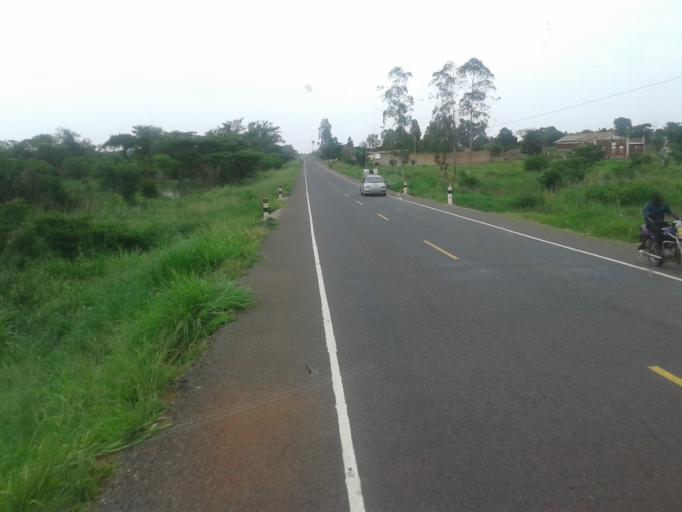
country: UG
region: Northern Region
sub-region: Oyam District
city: Oyam
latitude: 2.1681
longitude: 32.2209
